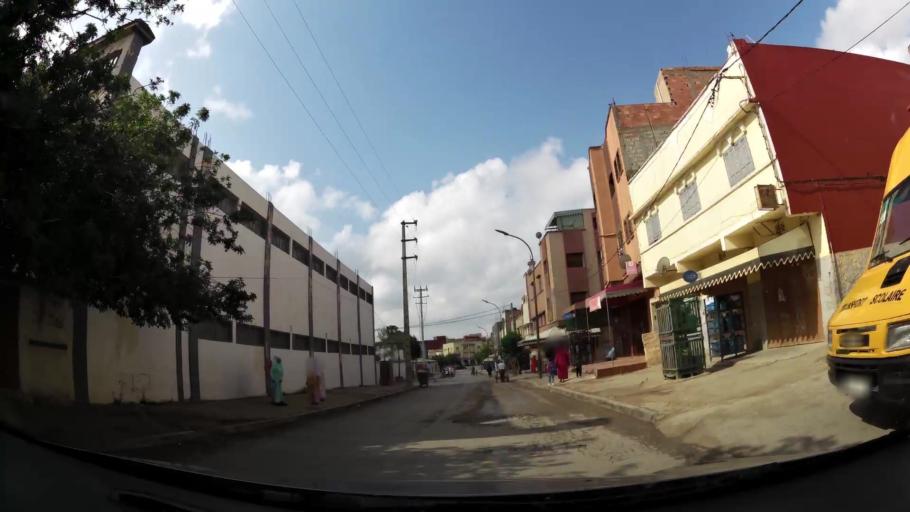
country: MA
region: Rabat-Sale-Zemmour-Zaer
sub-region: Khemisset
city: Tiflet
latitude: 33.8946
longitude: -6.3178
